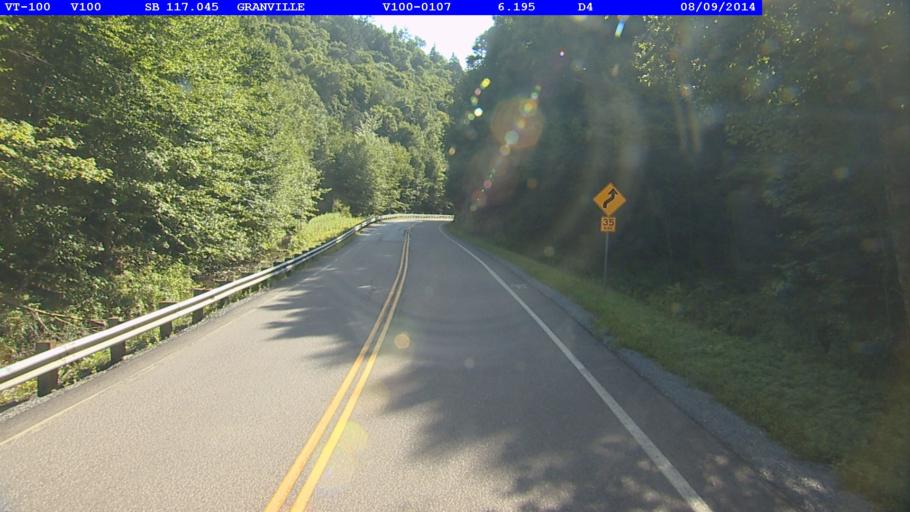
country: US
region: Vermont
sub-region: Orange County
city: Randolph
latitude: 44.0222
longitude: -72.8399
